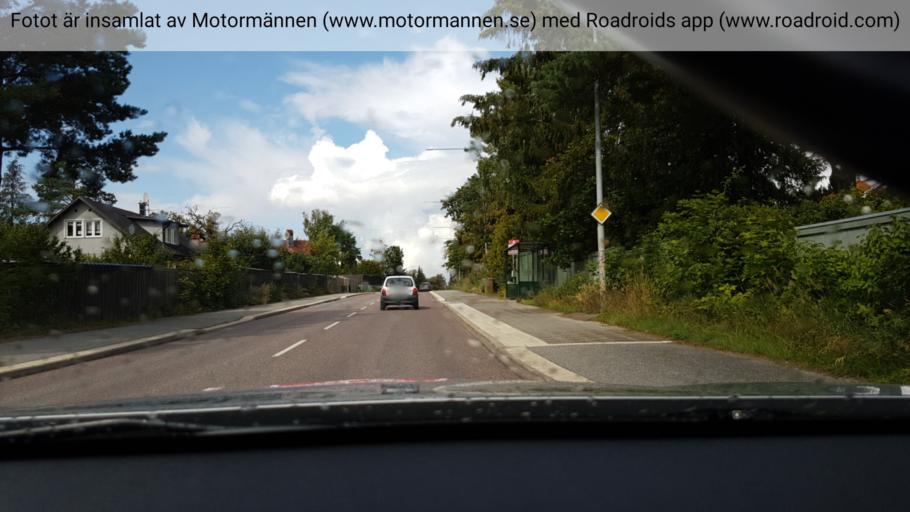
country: SE
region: Stockholm
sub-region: Huddinge Kommun
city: Segeltorp
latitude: 59.2686
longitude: 17.9575
